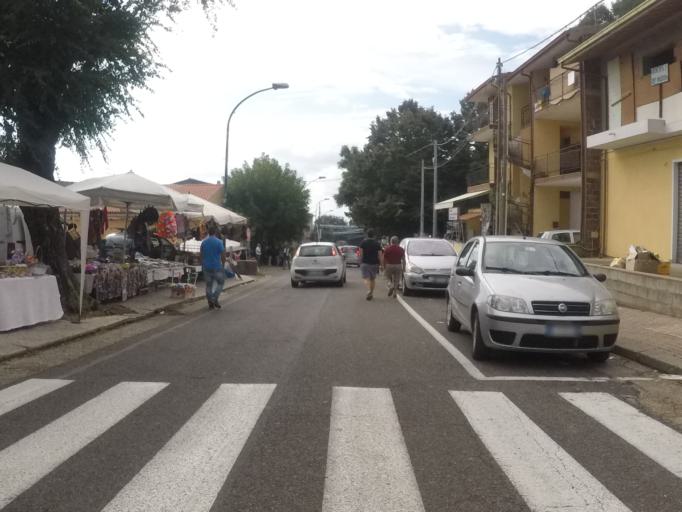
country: IT
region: Sardinia
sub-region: Provincia di Oristano
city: Bonarcado
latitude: 40.1013
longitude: 8.6544
